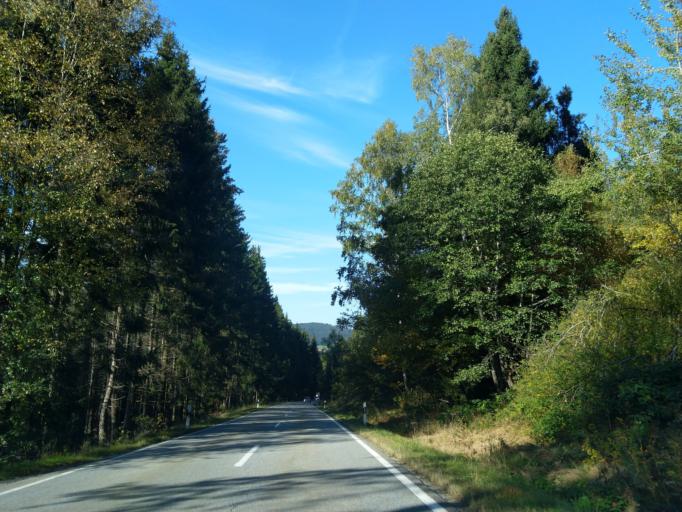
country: DE
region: Bavaria
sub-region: Lower Bavaria
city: Achslach
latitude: 48.9527
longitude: 12.9256
